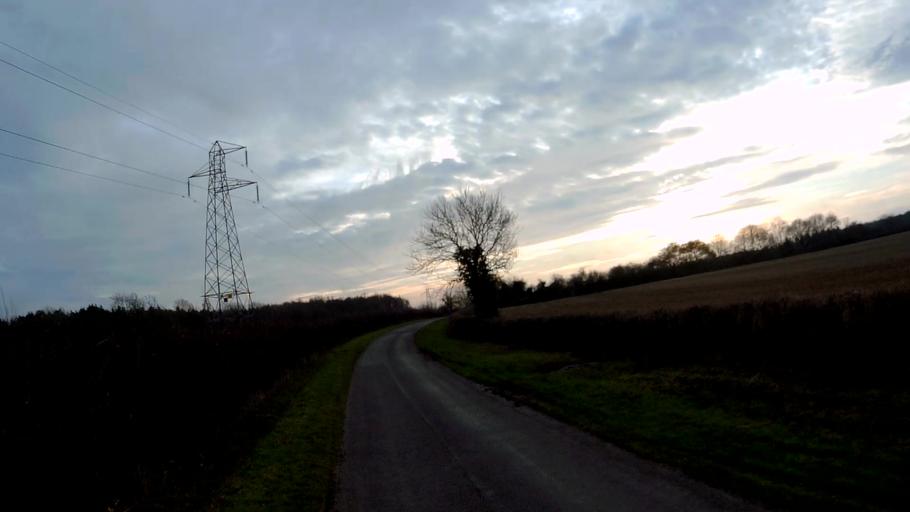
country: GB
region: England
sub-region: Lincolnshire
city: Bourne
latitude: 52.8250
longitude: -0.4055
